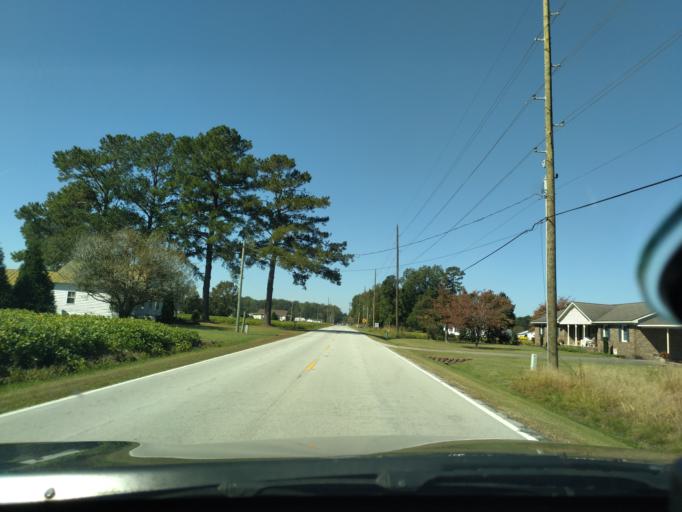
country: US
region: North Carolina
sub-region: Beaufort County
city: River Road
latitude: 35.5759
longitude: -76.9380
